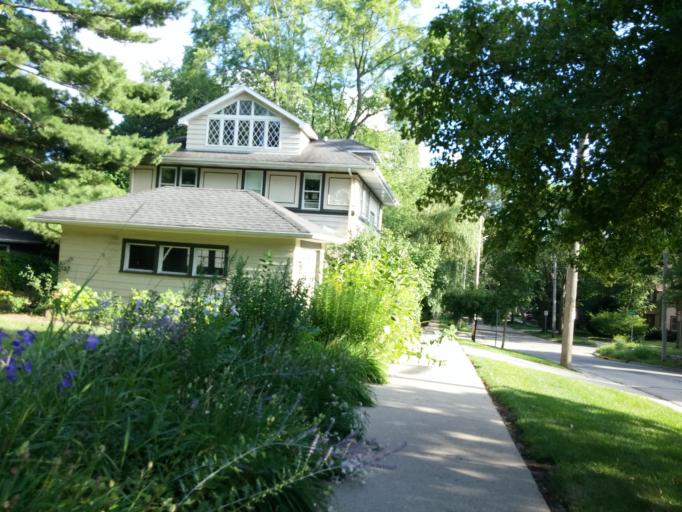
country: US
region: Wisconsin
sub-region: Dane County
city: Madison
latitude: 43.0675
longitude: -89.4212
